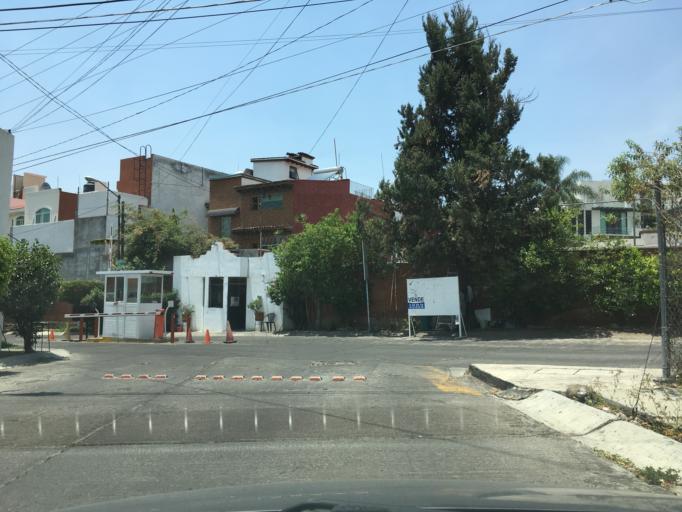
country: MX
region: Michoacan
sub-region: Morelia
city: Puerto de Buenavista (Lazaro Cardenas)
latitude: 19.6897
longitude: -101.1457
